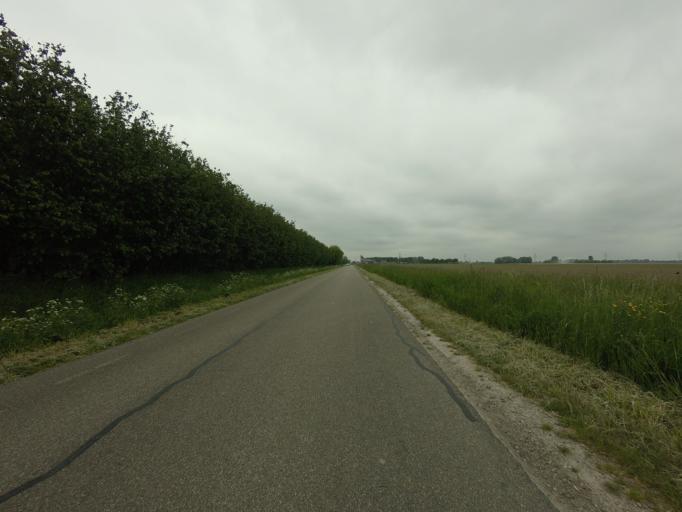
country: NL
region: South Holland
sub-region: Gemeente Spijkenisse
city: Spijkenisse
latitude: 51.8001
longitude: 4.3434
